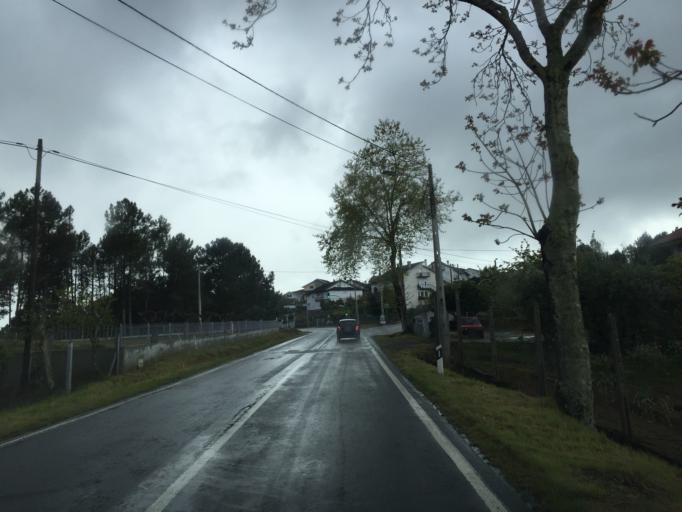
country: PT
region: Guarda
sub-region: Seia
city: Seia
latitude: 40.3863
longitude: -7.7549
